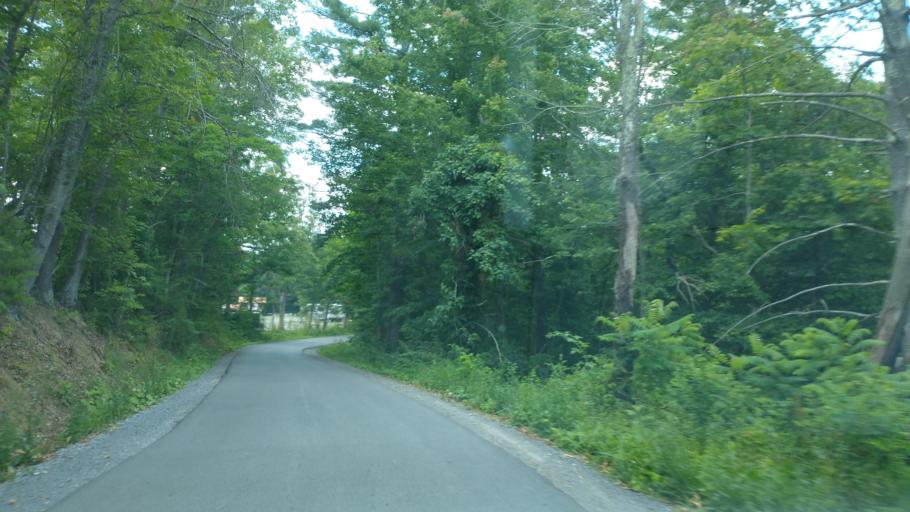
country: US
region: West Virginia
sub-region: Mercer County
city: Athens
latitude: 37.4510
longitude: -81.0619
